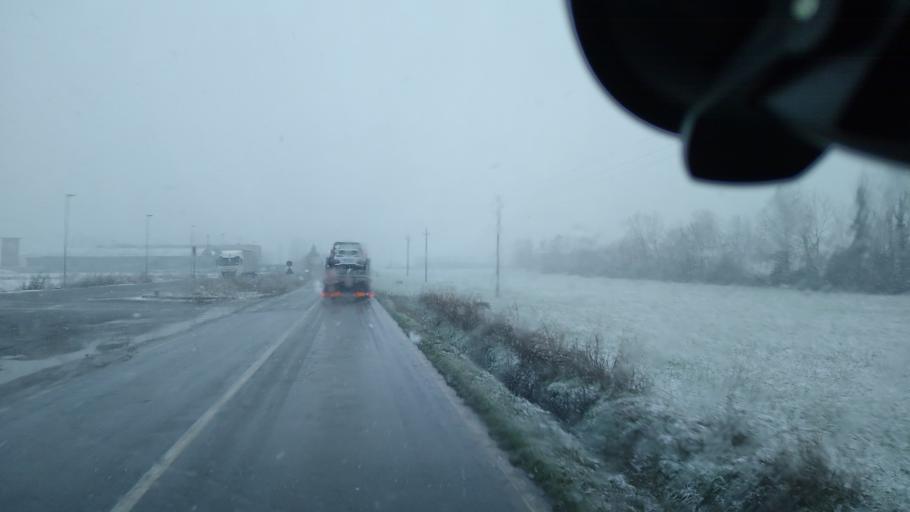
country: IT
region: Lombardy
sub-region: Provincia di Bergamo
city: Bariano
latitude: 45.4980
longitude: 9.6975
